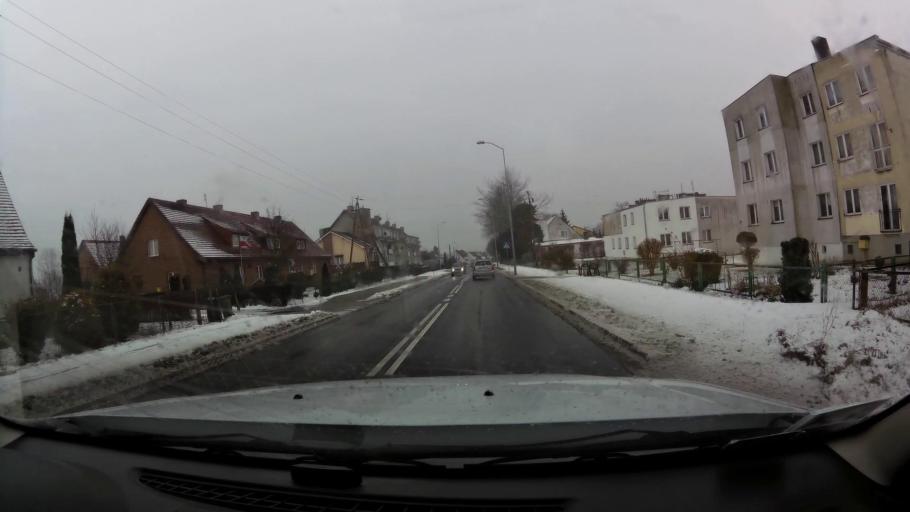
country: PL
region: West Pomeranian Voivodeship
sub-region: Powiat gryficki
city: Trzebiatow
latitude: 54.0778
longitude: 15.2570
